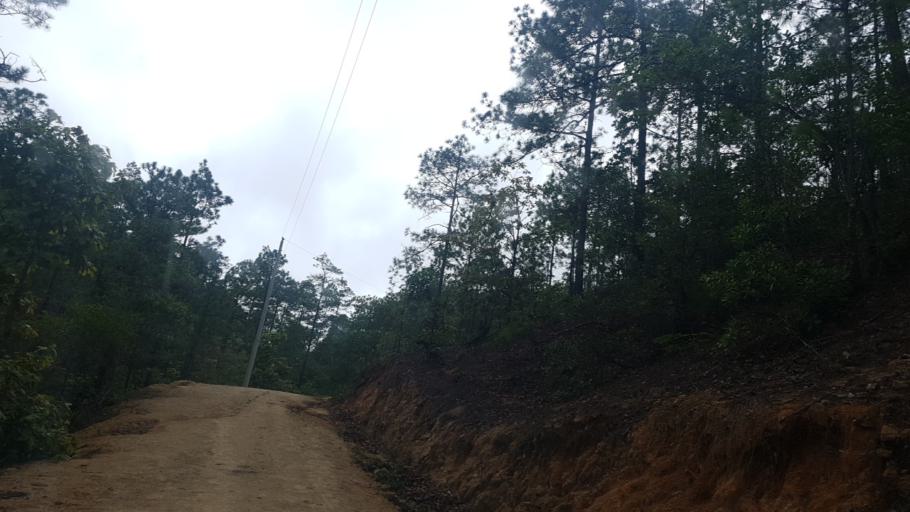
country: NI
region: Madriz
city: Totogalpa
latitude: 13.6147
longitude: -86.6110
